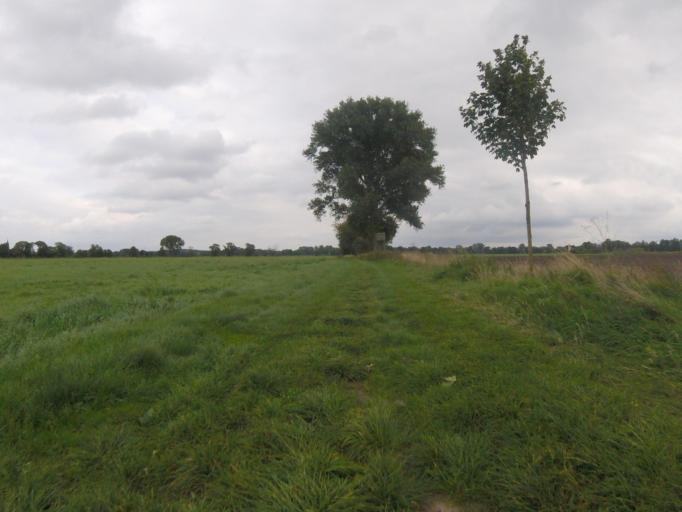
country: DE
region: Brandenburg
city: Mittenwalde
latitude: 52.2595
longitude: 13.5158
